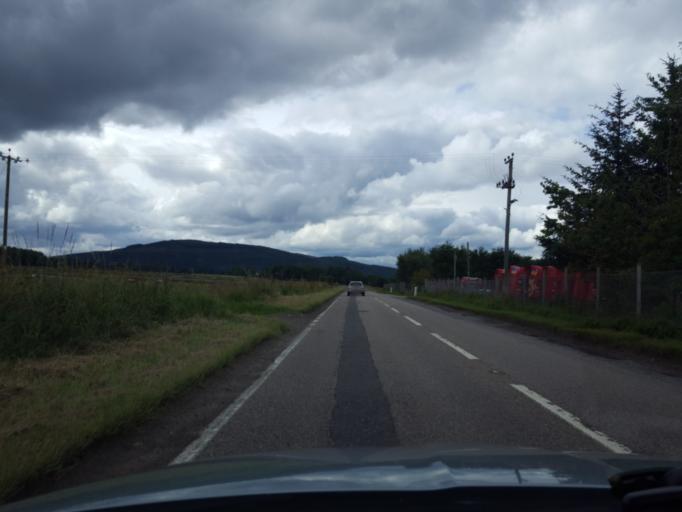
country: GB
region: Scotland
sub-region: Moray
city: Rothes
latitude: 57.4277
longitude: -3.3459
